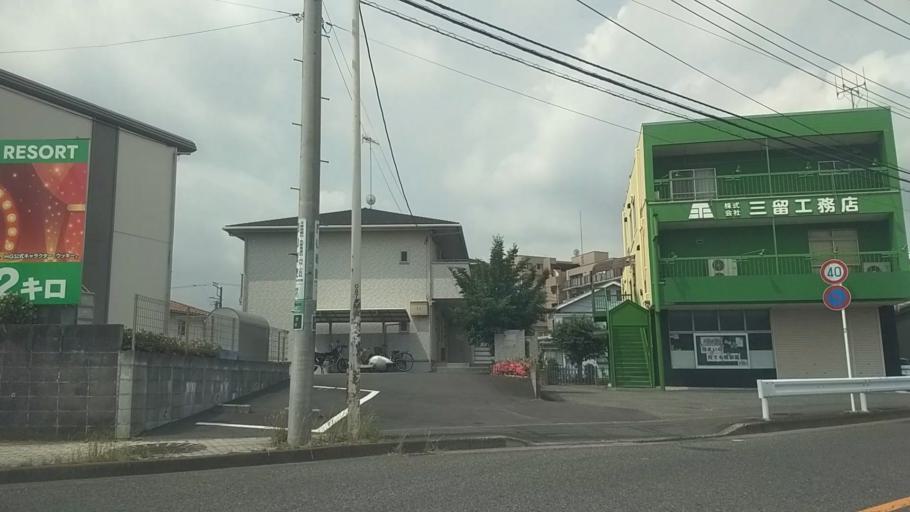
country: JP
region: Kanagawa
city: Fujisawa
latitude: 35.3646
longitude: 139.4788
